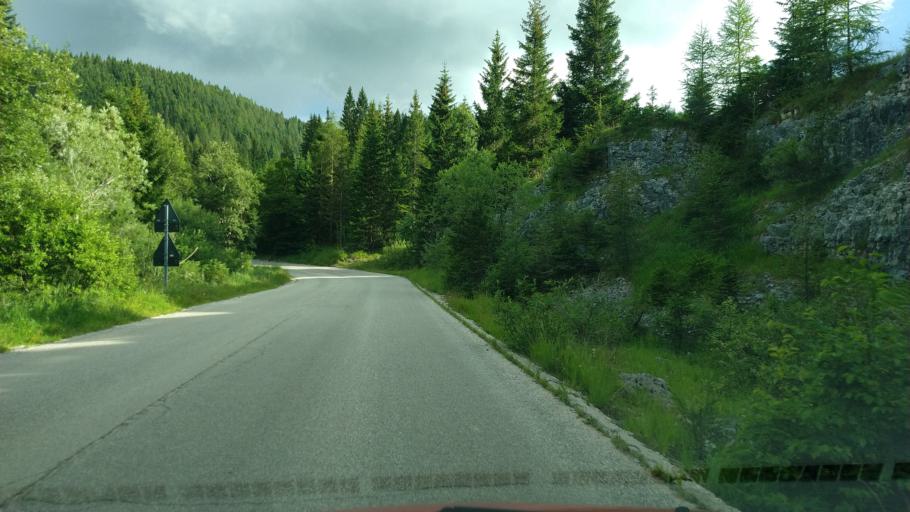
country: IT
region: Veneto
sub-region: Provincia di Vicenza
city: Lastebasse
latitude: 45.8941
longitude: 11.2666
